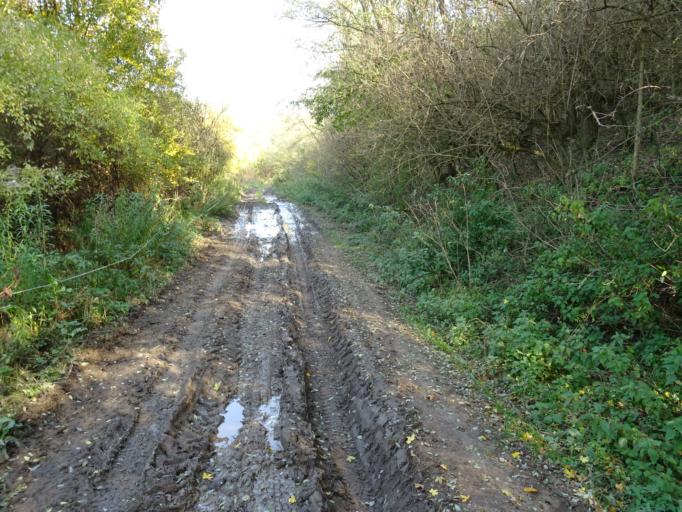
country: HU
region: Nograd
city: Salgotarjan
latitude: 48.0925
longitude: 19.7523
